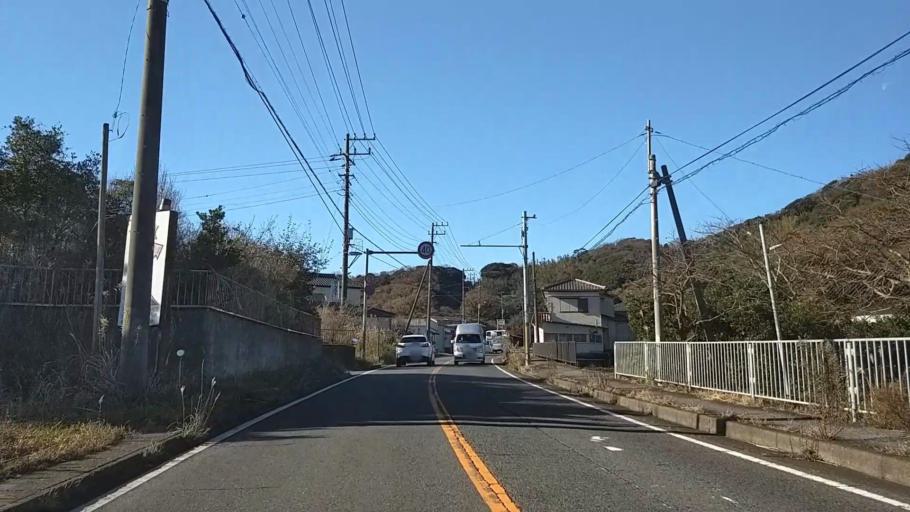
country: JP
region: Chiba
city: Futtsu
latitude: 35.2050
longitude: 139.8436
